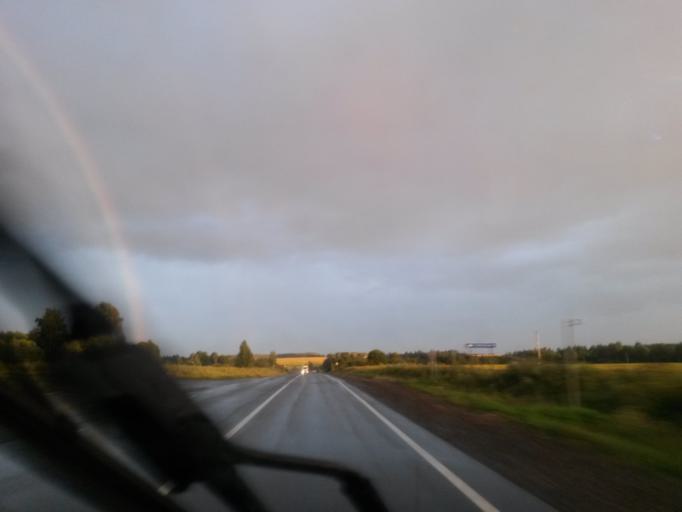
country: RU
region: Jaroslavl
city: Gavrilov-Yam
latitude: 57.3332
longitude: 39.9207
